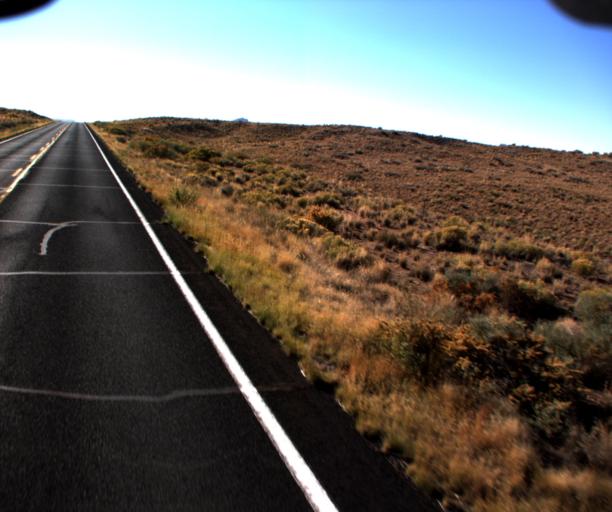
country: US
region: Arizona
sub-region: Navajo County
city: Dilkon
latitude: 35.5556
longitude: -110.4547
